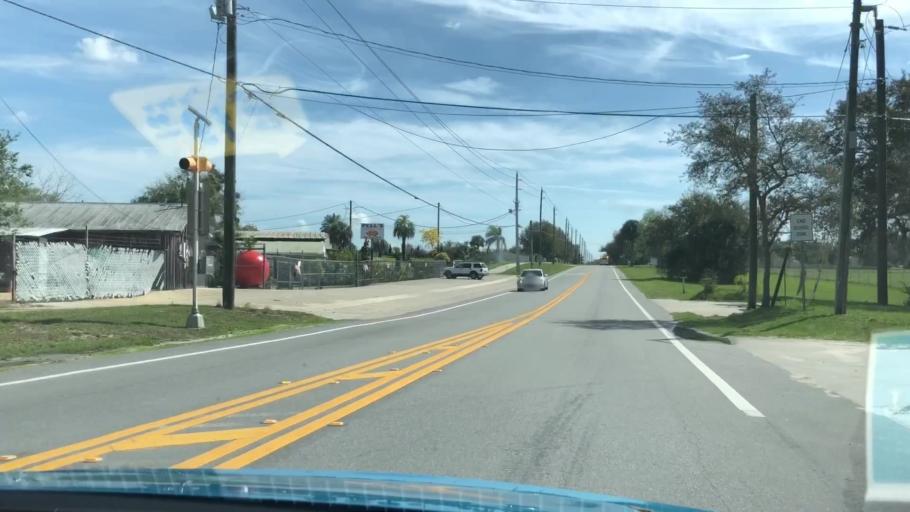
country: US
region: Florida
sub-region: Seminole County
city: Midway
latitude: 28.8527
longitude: -81.1740
